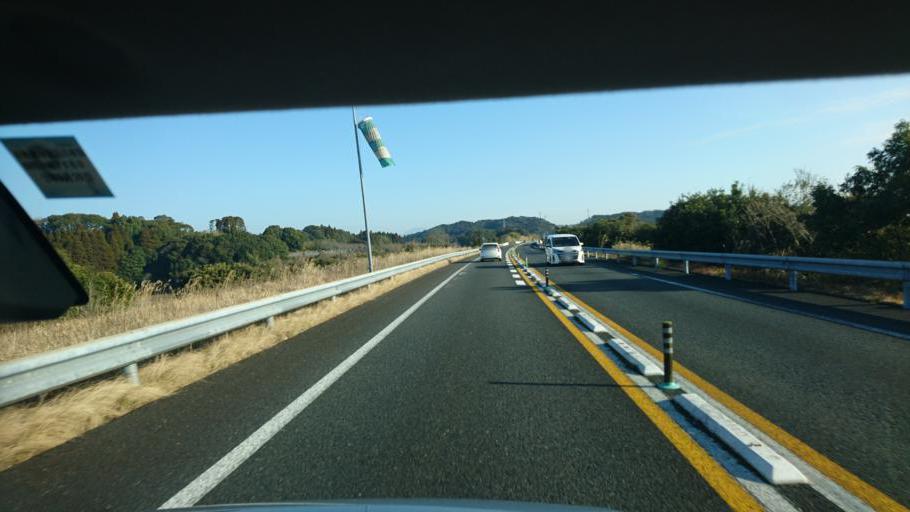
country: JP
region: Miyazaki
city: Miyazaki-shi
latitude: 31.9530
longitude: 131.3542
